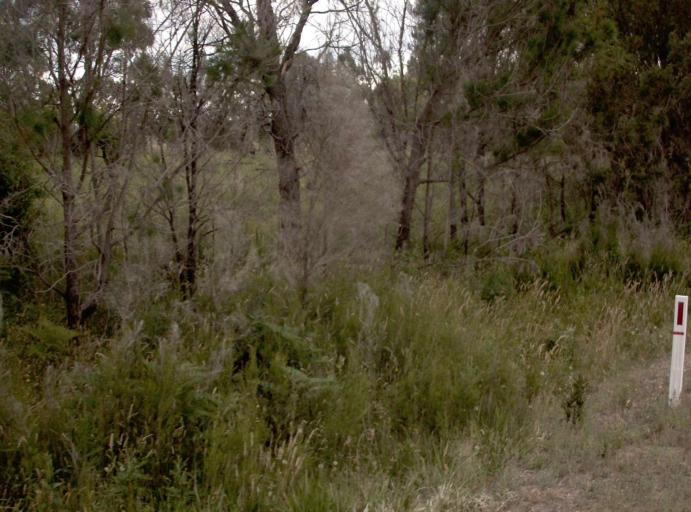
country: AU
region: Victoria
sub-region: East Gippsland
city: Bairnsdale
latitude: -37.9711
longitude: 147.4722
